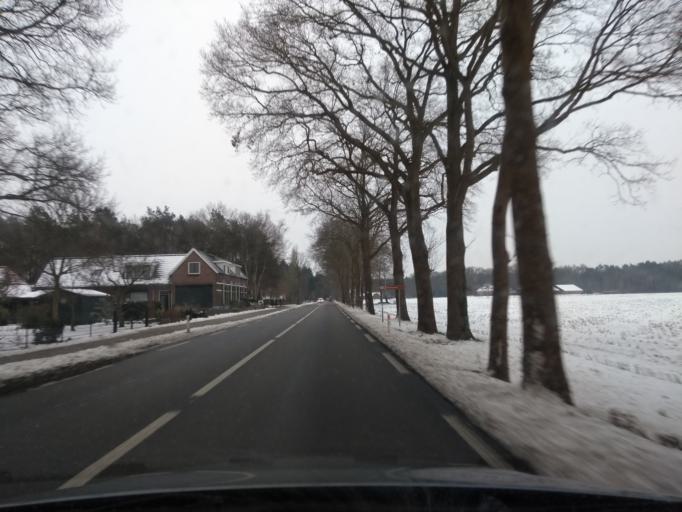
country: NL
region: Gelderland
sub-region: Gemeente Lochem
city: Barchem
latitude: 52.1058
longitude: 6.4475
